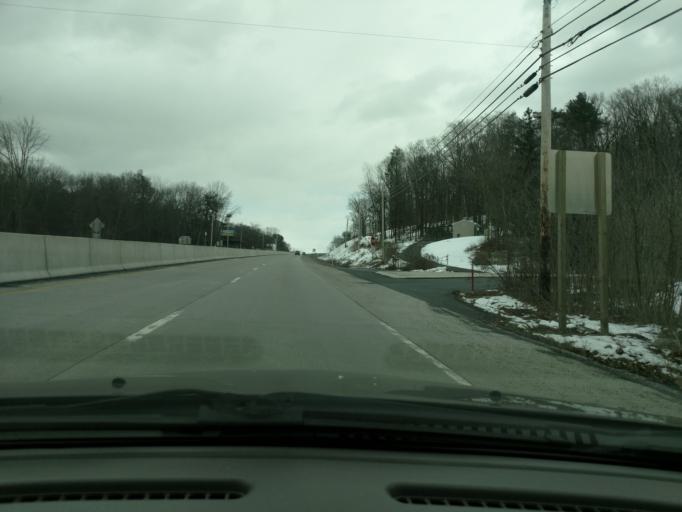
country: US
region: Pennsylvania
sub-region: Schuylkill County
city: Orwigsburg
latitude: 40.6174
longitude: -76.0509
